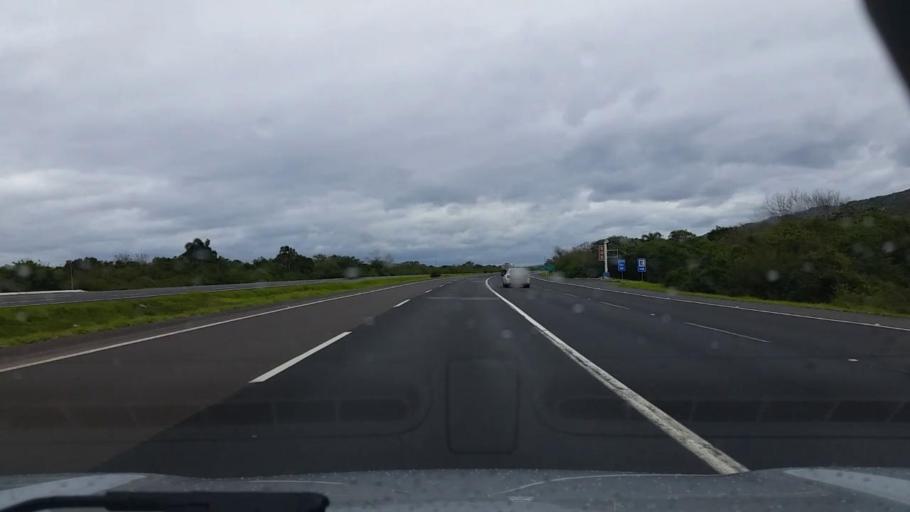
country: BR
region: Rio Grande do Sul
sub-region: Osorio
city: Osorio
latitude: -29.8971
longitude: -50.2919
